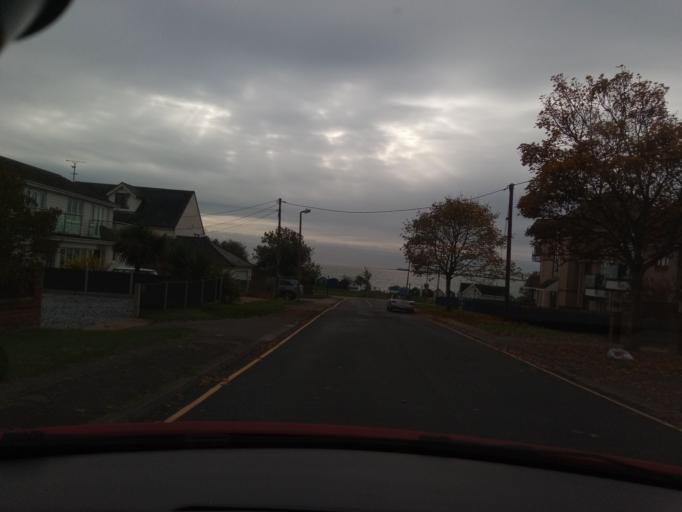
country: GB
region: England
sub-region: Essex
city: West Mersea
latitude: 51.7751
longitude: 0.9290
